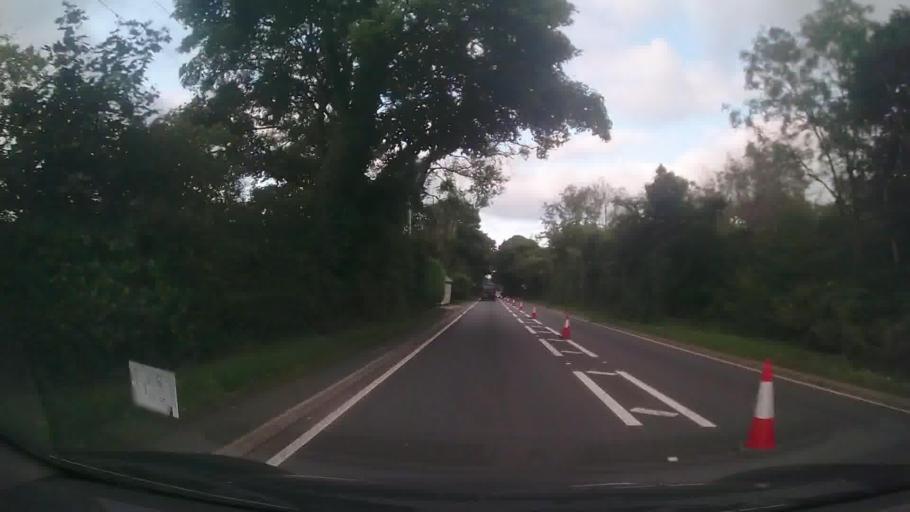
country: GB
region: Wales
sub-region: Pembrokeshire
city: Jeffreyston
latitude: 51.7202
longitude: -4.7516
